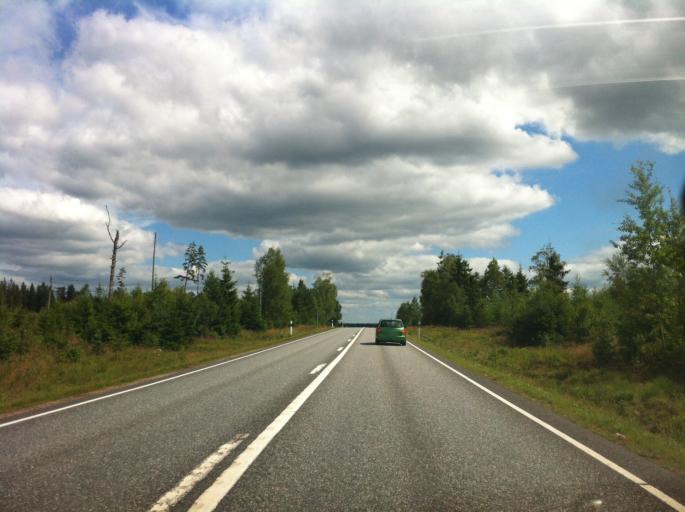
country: SE
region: Joenkoeping
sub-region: Gislaveds Kommun
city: Gislaved
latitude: 57.2641
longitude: 13.4852
